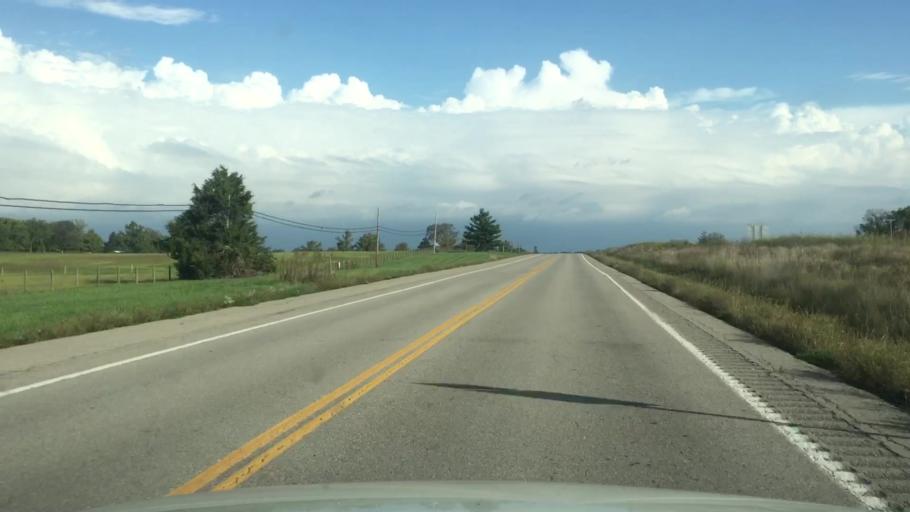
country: US
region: Missouri
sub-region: Boone County
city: Ashland
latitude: 38.8366
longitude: -92.2494
